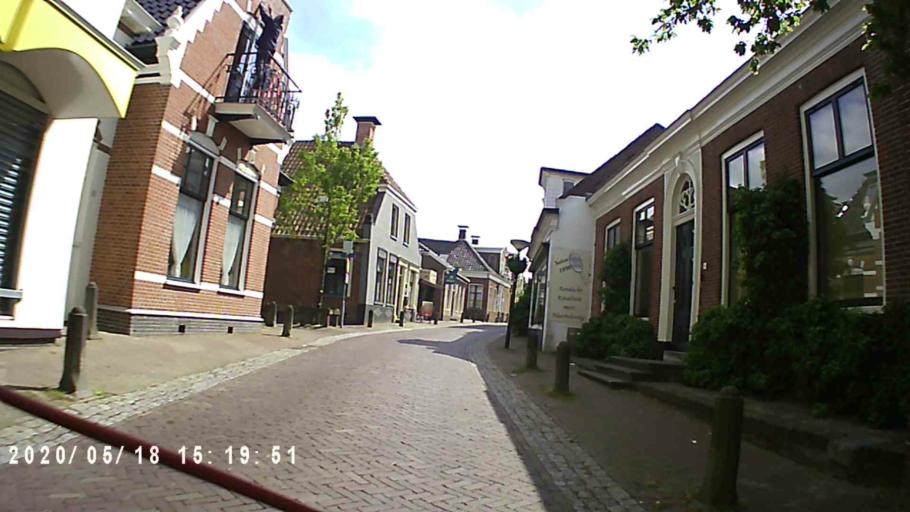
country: NL
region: Groningen
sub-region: Gemeente Winsum
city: Winsum
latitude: 53.3316
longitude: 6.5156
